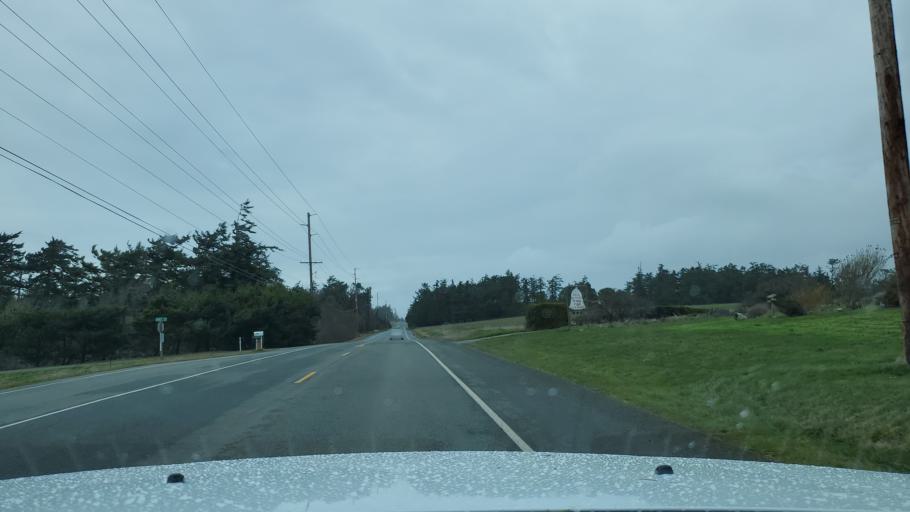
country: US
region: Washington
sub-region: Island County
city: Coupeville
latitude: 48.2424
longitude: -122.7517
